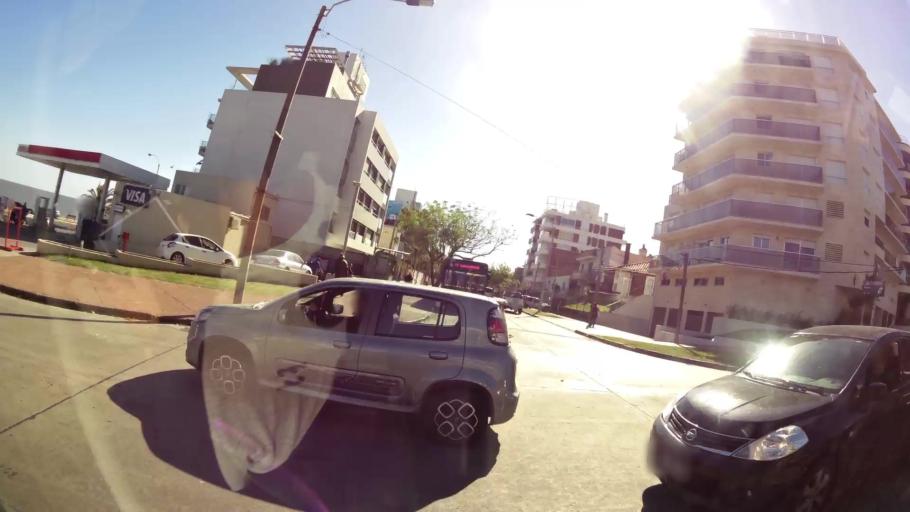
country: UY
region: Canelones
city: Paso de Carrasco
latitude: -34.8946
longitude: -56.0917
